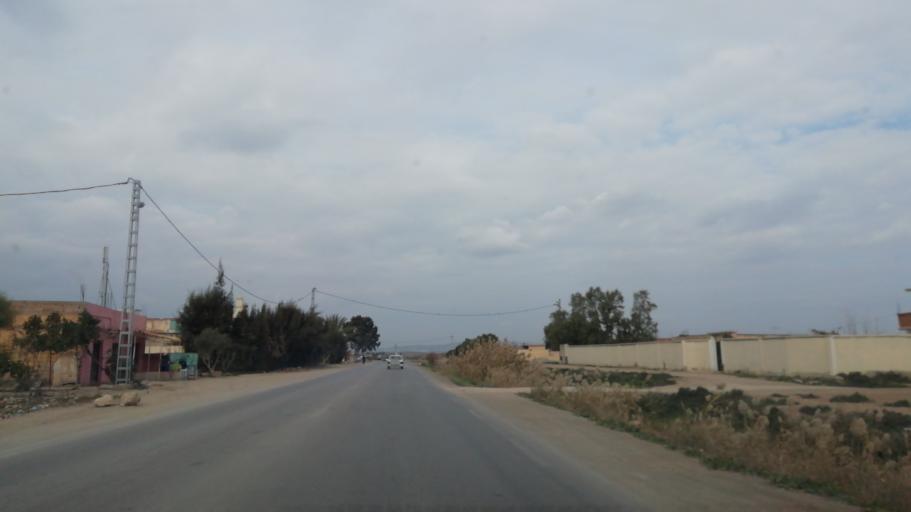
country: DZ
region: Mostaganem
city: Mostaganem
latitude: 35.6977
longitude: 0.0554
